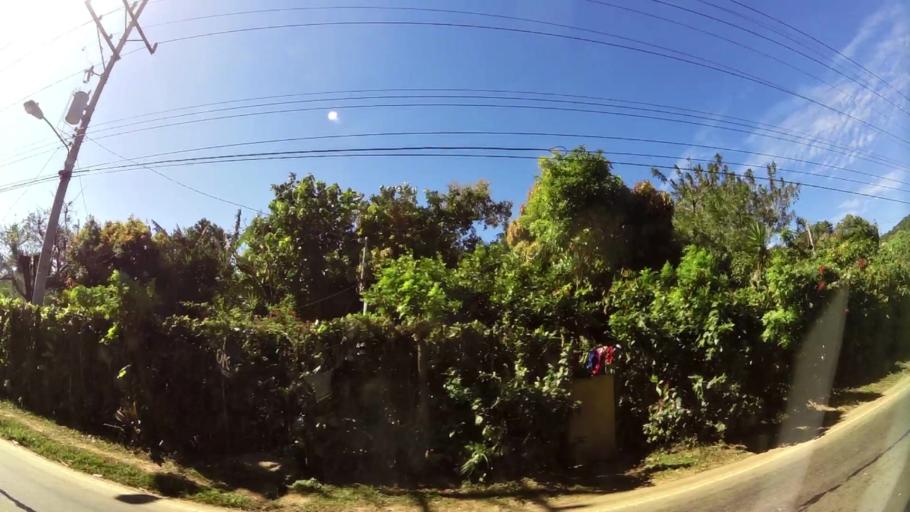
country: SV
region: Sonsonate
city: Juayua
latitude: 13.8357
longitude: -89.7637
